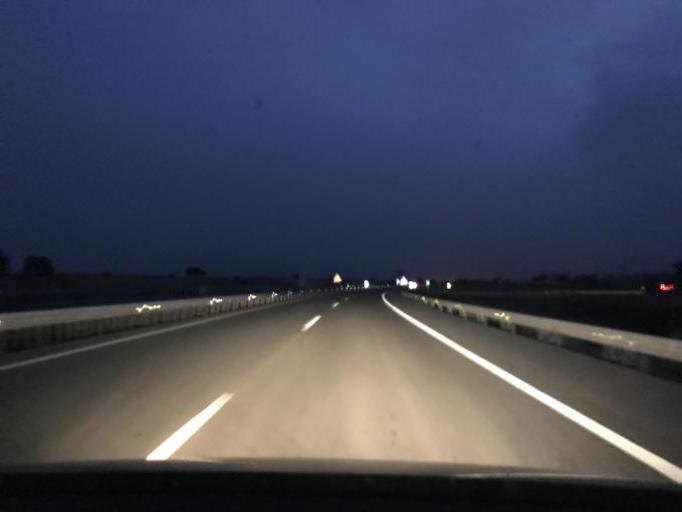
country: ES
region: Andalusia
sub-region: Provincia de Granada
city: Benalua de Guadix
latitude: 37.3685
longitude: -3.0721
